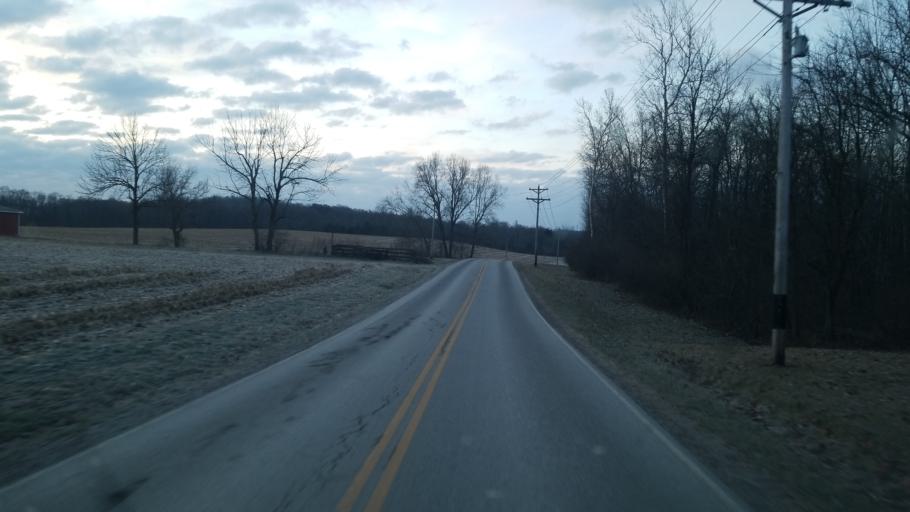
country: US
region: Ohio
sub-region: Highland County
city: Leesburg
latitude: 39.2671
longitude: -83.4740
